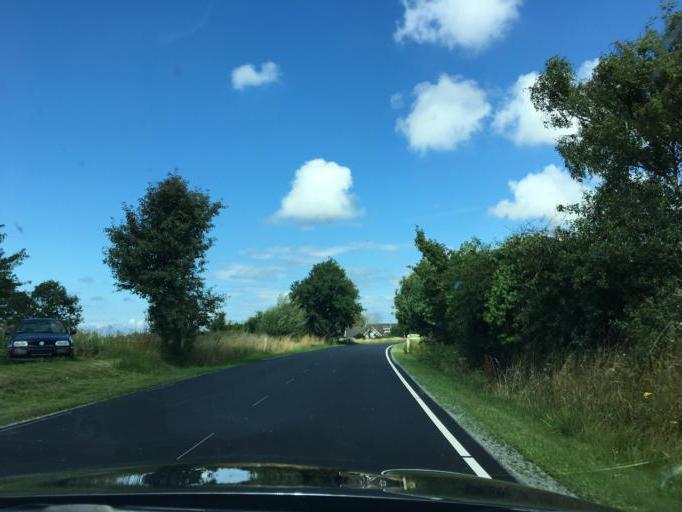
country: DK
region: Capital Region
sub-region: Gribskov Kommune
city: Helsinge
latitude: 56.0692
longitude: 12.1990
